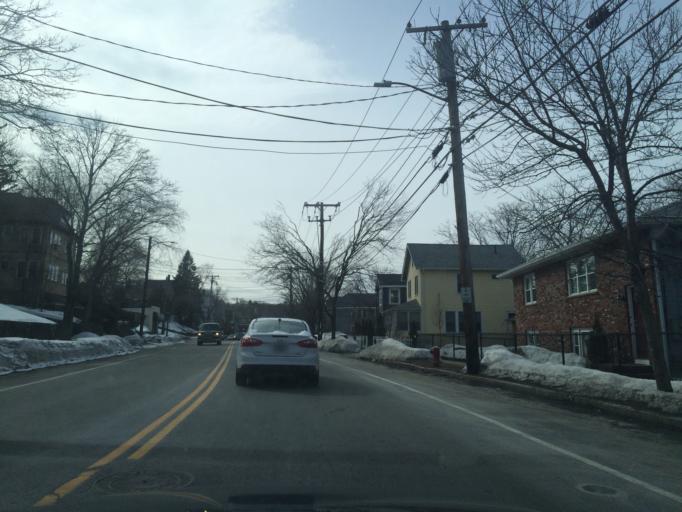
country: US
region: Massachusetts
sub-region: Middlesex County
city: Belmont
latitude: 42.4254
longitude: -71.1898
